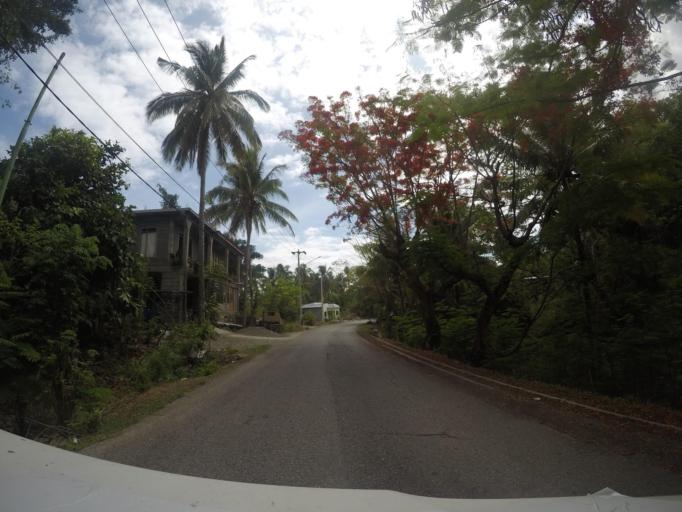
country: TL
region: Baucau
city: Baucau
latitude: -8.4618
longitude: 126.4461
